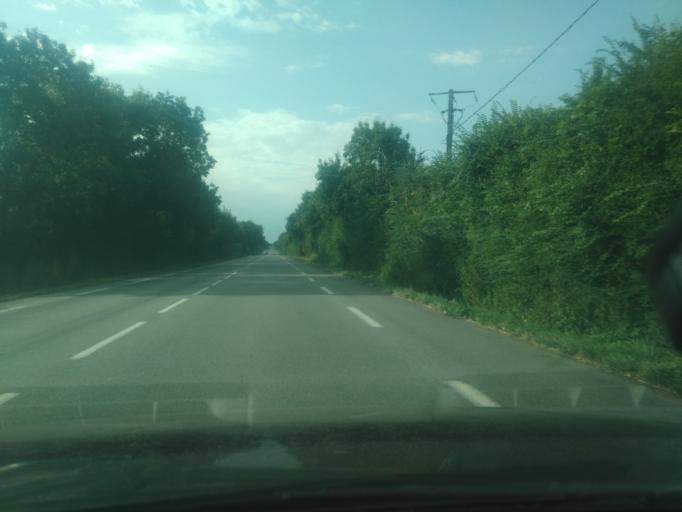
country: FR
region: Pays de la Loire
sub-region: Departement de la Vendee
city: Chantonnay
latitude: 46.7168
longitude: -1.0702
